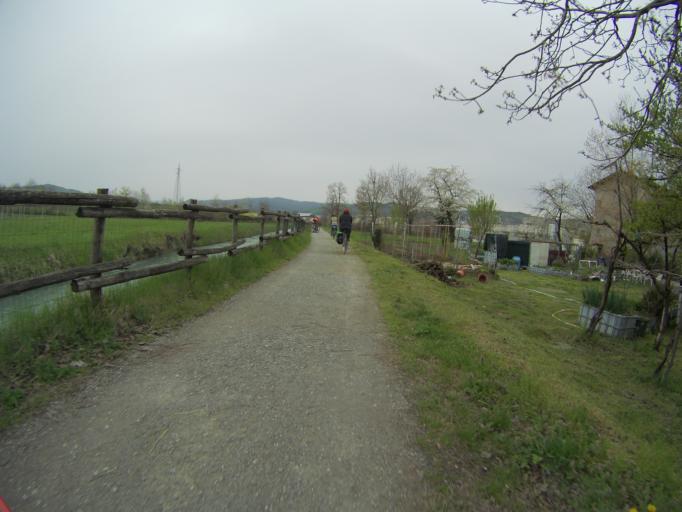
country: IT
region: Emilia-Romagna
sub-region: Provincia di Reggio Emilia
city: Ciano d'Enza
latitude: 44.6118
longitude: 10.4106
